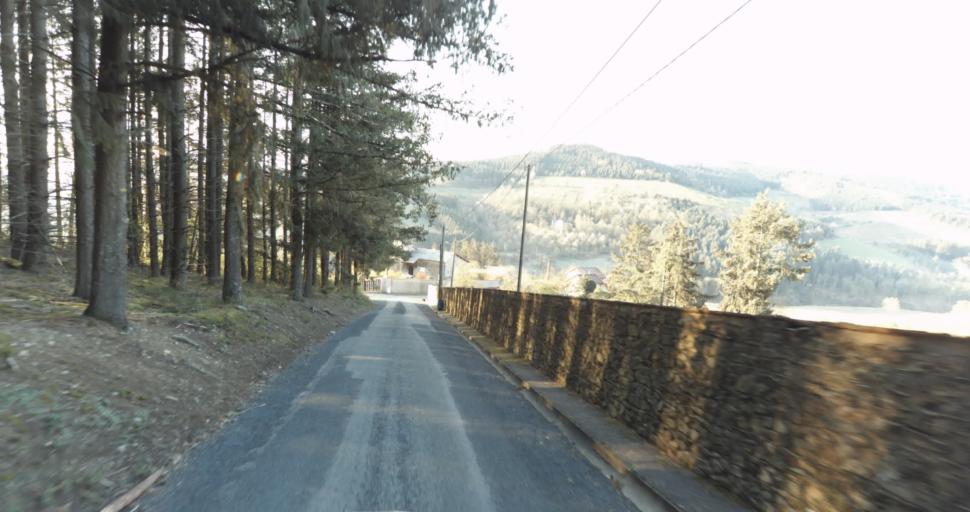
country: FR
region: Rhone-Alpes
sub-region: Departement du Rhone
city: Tarare
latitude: 45.8980
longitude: 4.4217
